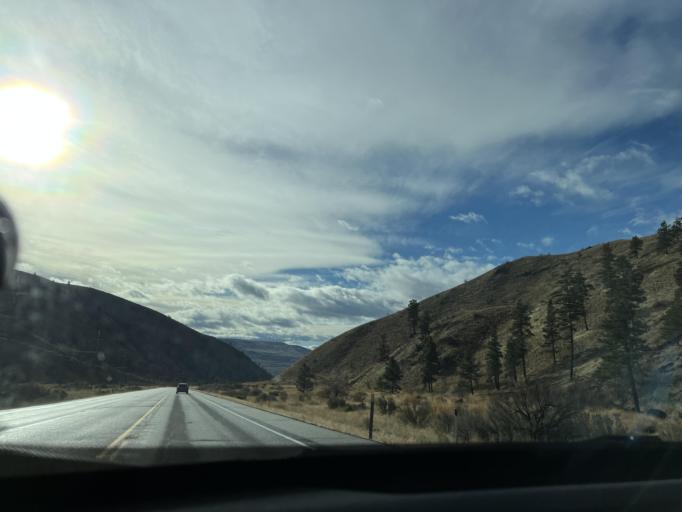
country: US
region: Washington
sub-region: Chelan County
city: Manson
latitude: 47.8023
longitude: -120.1329
